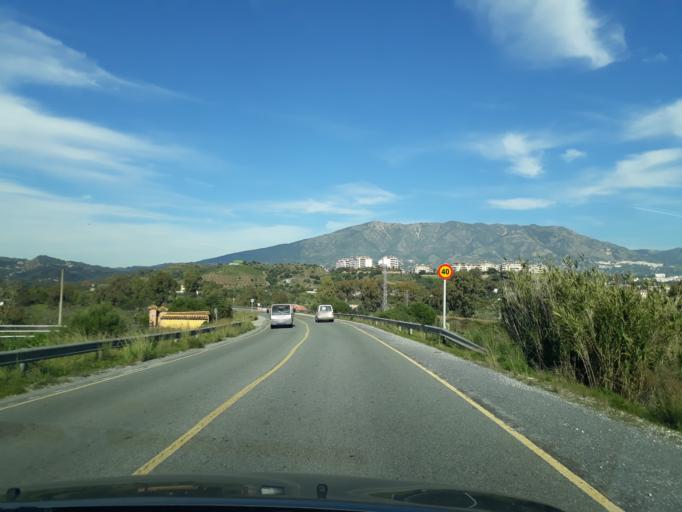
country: ES
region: Andalusia
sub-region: Provincia de Malaga
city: Fuengirola
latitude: 36.5413
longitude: -4.6871
